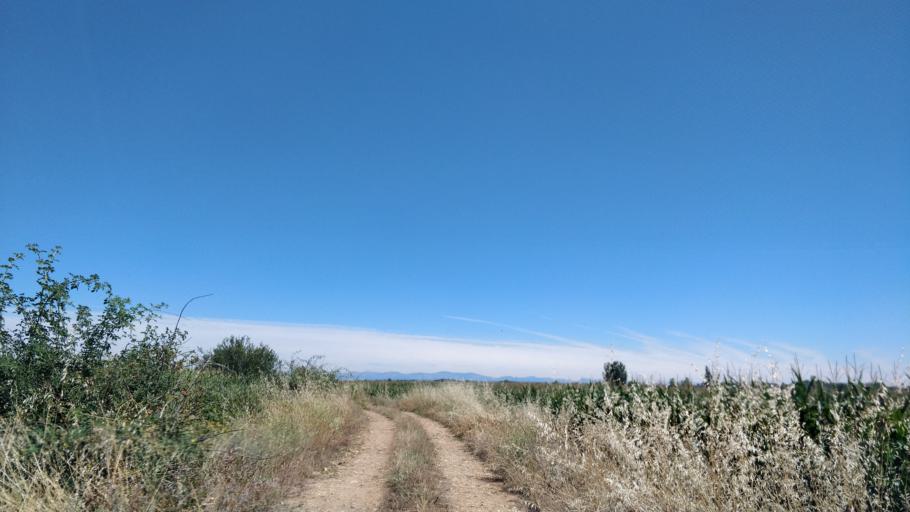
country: ES
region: Castille and Leon
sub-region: Provincia de Leon
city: Bustillo del Paramo
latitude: 42.4466
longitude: -5.8153
